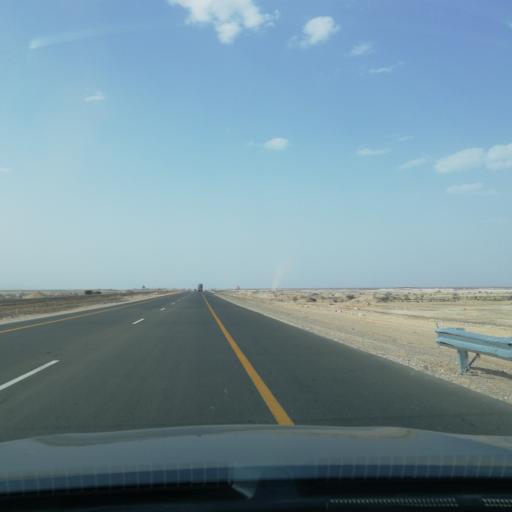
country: OM
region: Muhafazat ad Dakhiliyah
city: Adam
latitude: 22.0606
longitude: 57.5130
